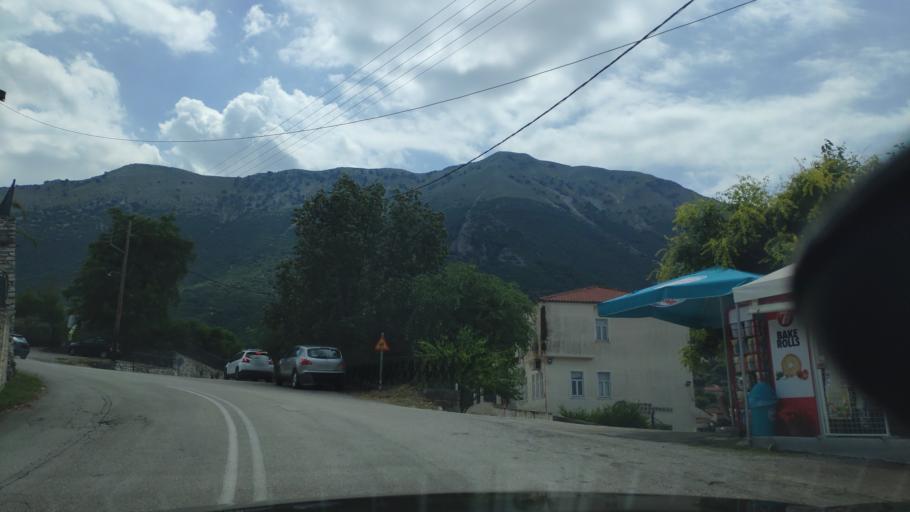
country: GR
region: Epirus
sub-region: Nomos Artas
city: Kampi
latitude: 39.2709
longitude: 20.9412
